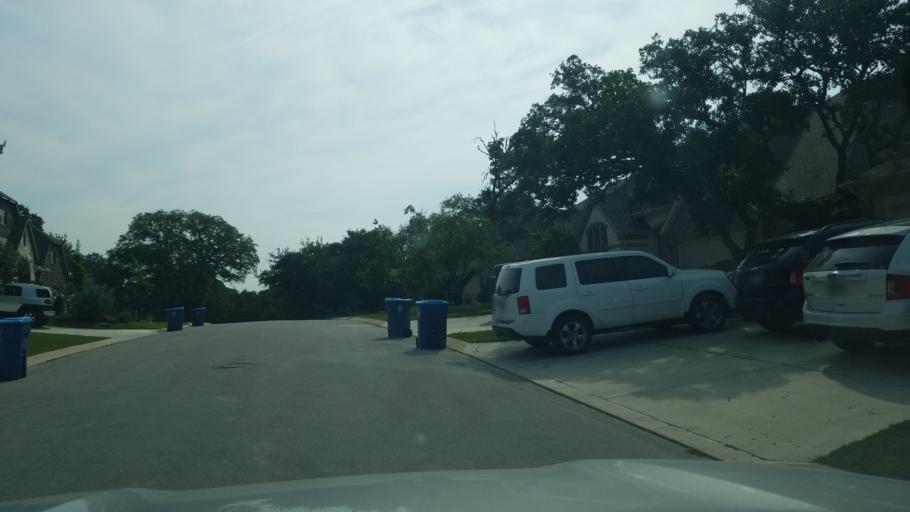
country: US
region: Texas
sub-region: Bexar County
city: Scenic Oaks
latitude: 29.7255
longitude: -98.6606
